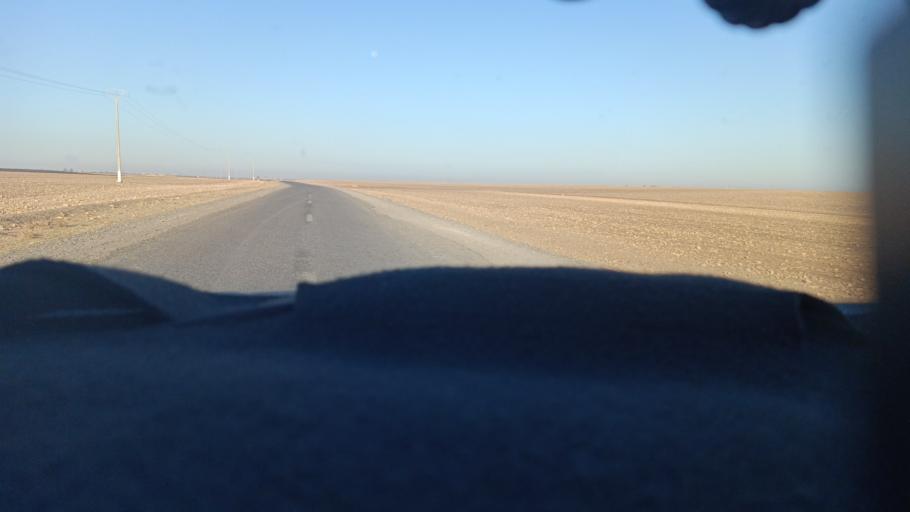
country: MA
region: Doukkala-Abda
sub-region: Safi
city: Youssoufia
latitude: 32.3712
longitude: -8.6834
